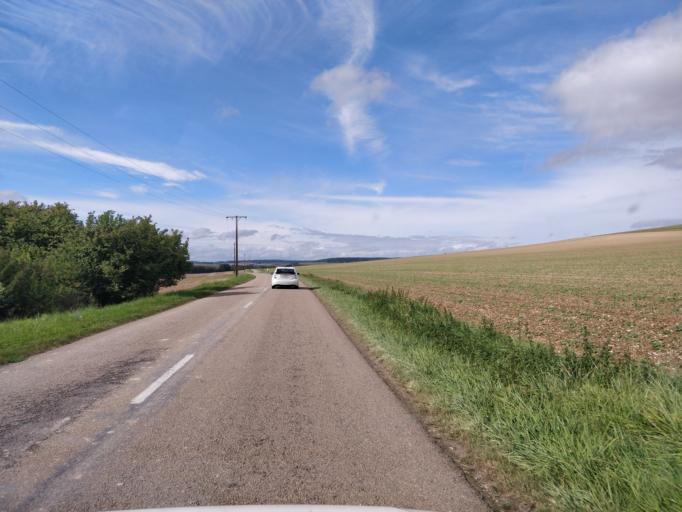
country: FR
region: Champagne-Ardenne
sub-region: Departement de l'Aube
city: Aix-en-Othe
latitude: 48.2137
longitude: 3.6249
